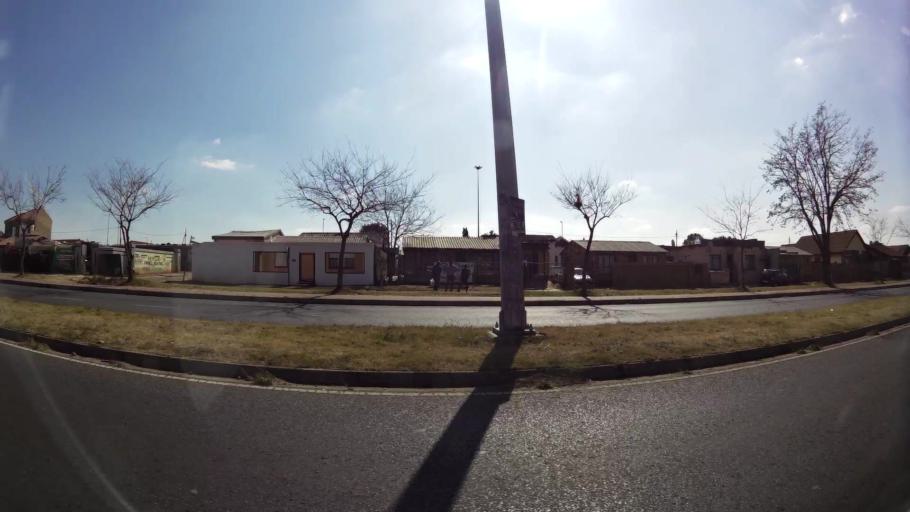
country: ZA
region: Gauteng
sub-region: City of Johannesburg Metropolitan Municipality
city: Soweto
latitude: -26.2759
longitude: 27.8688
